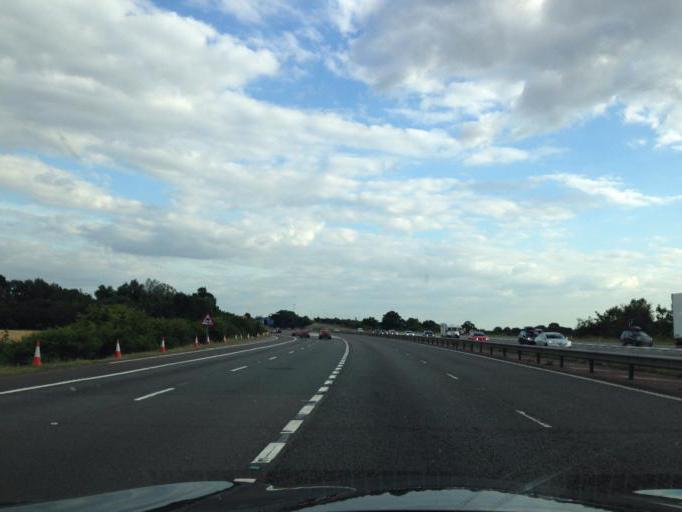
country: GB
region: England
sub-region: Oxfordshire
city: Bicester
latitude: 51.8744
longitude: -1.2007
